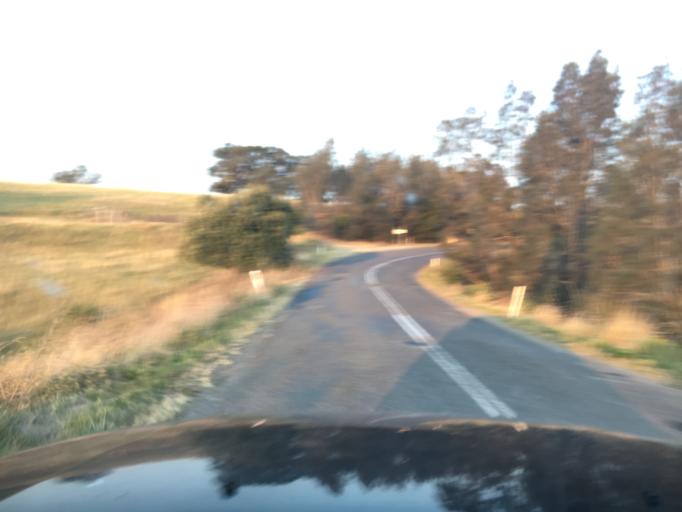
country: AU
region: New South Wales
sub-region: Cessnock
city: Branxton
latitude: -32.6121
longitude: 151.3480
